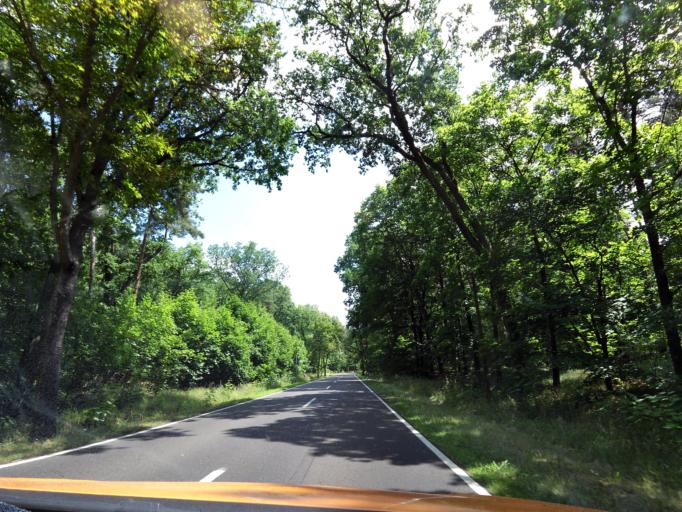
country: DE
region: Brandenburg
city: Nauen
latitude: 52.6293
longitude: 12.9316
